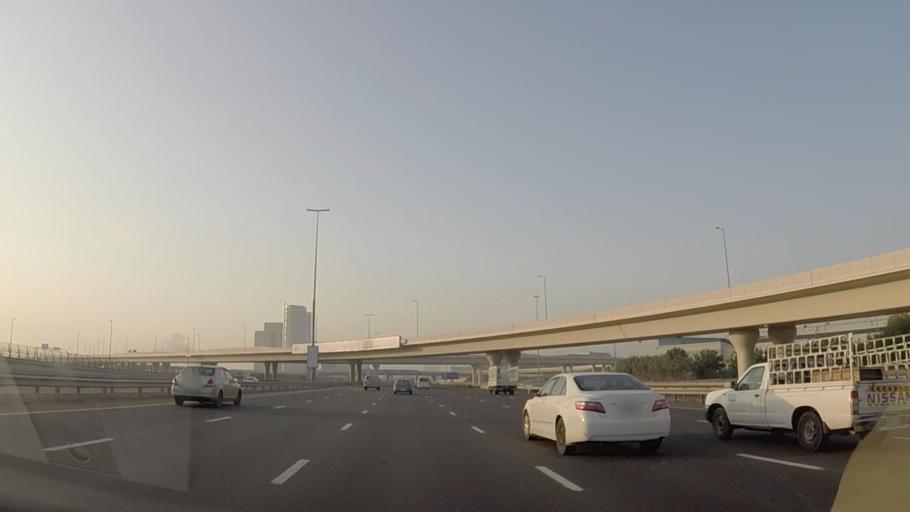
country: AE
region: Dubai
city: Dubai
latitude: 24.9924
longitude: 55.0936
